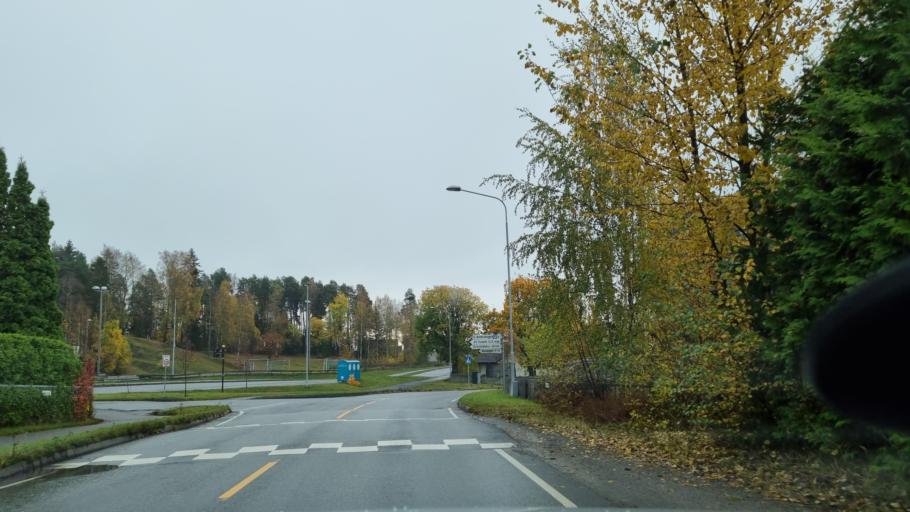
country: NO
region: Hedmark
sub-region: Hamar
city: Hamar
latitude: 60.8028
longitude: 11.0632
